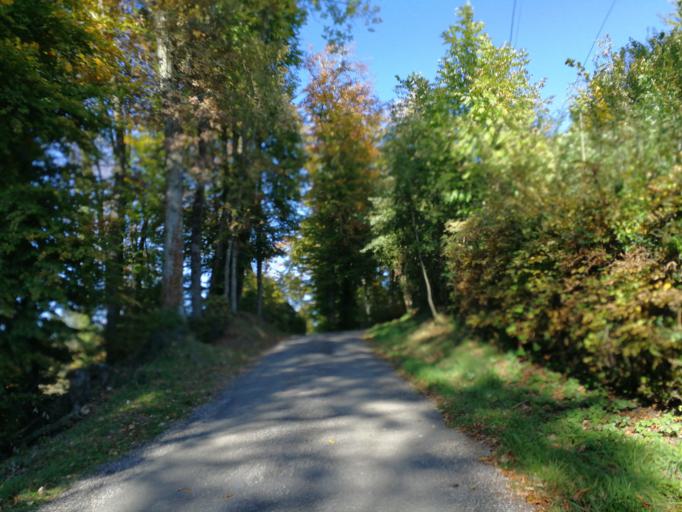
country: CH
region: Zurich
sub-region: Bezirk Hinwil
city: Wolfhausen
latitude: 47.2485
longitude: 8.7947
